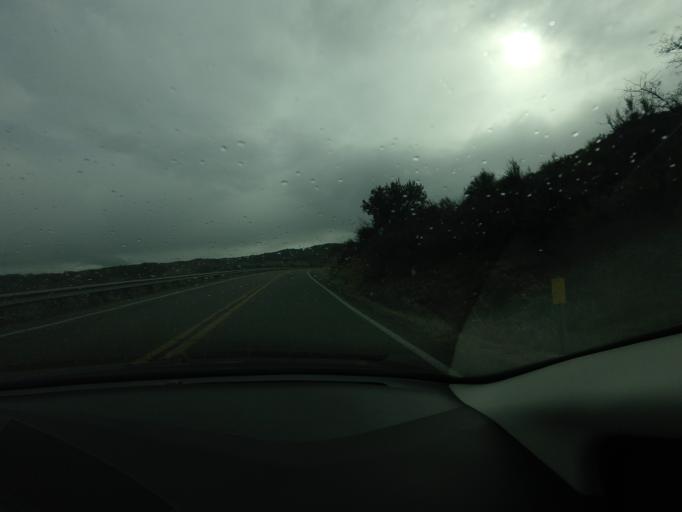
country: US
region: Arizona
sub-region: Yavapai County
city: Lake Montezuma
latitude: 34.6563
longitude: -111.8223
